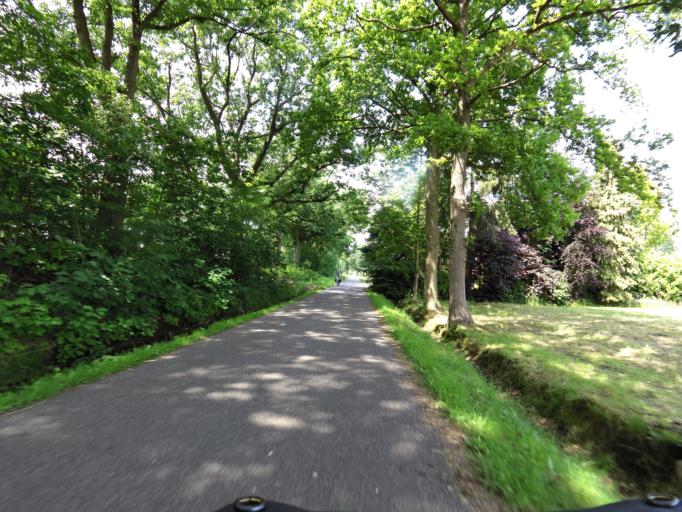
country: NL
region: Gelderland
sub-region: Gemeente Apeldoorn
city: Loenen
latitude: 52.1531
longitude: 6.0319
